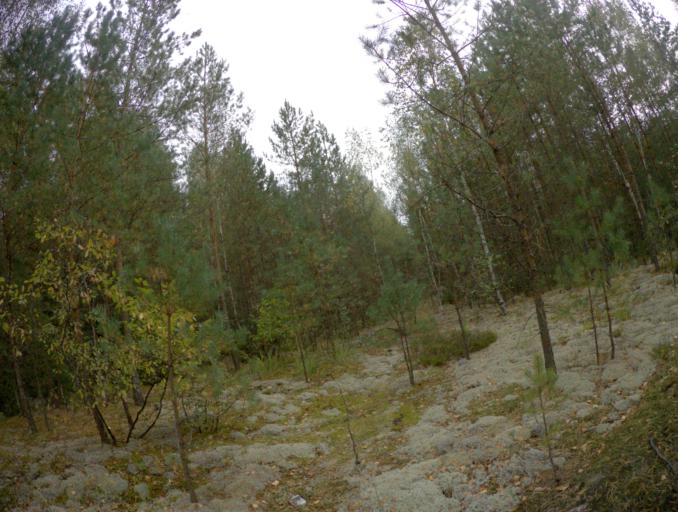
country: RU
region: Vladimir
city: Golovino
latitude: 55.8698
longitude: 40.4068
